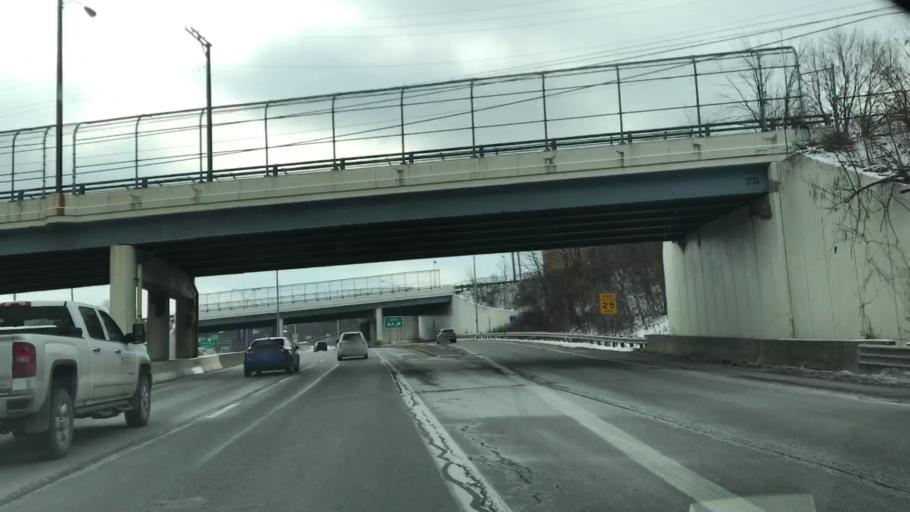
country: US
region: Ohio
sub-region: Mahoning County
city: Youngstown
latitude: 41.0949
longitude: -80.6567
